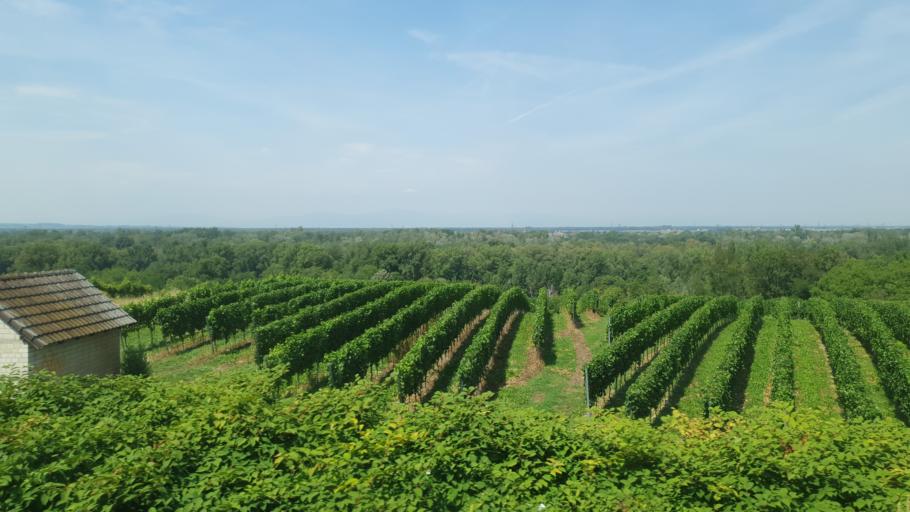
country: DE
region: Baden-Wuerttemberg
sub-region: Freiburg Region
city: Bad Bellingen
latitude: 47.7158
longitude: 7.5432
